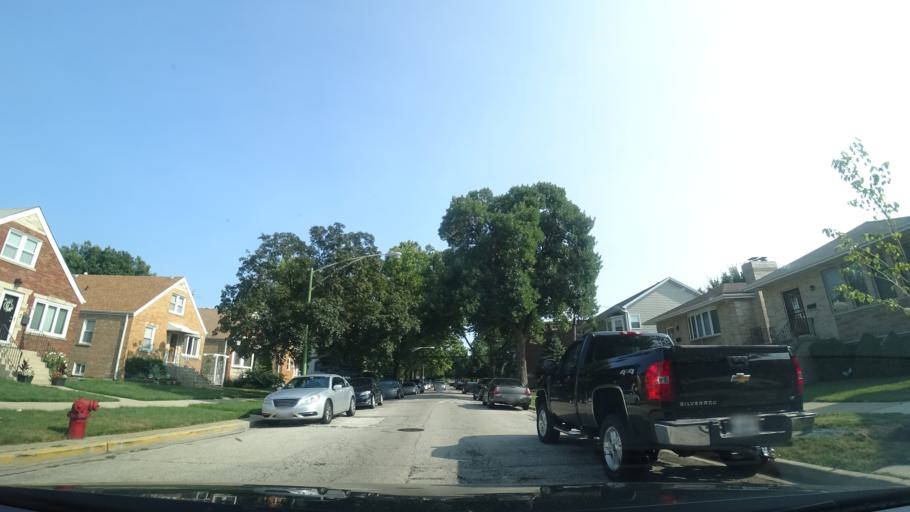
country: US
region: Illinois
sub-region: Cook County
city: Harwood Heights
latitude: 41.9731
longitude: -87.7818
